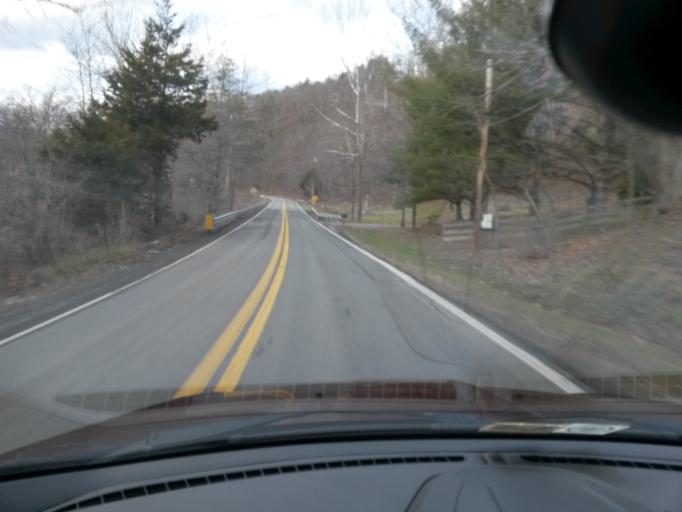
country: US
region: West Virginia
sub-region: Monroe County
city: Union
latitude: 37.5081
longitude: -80.6091
